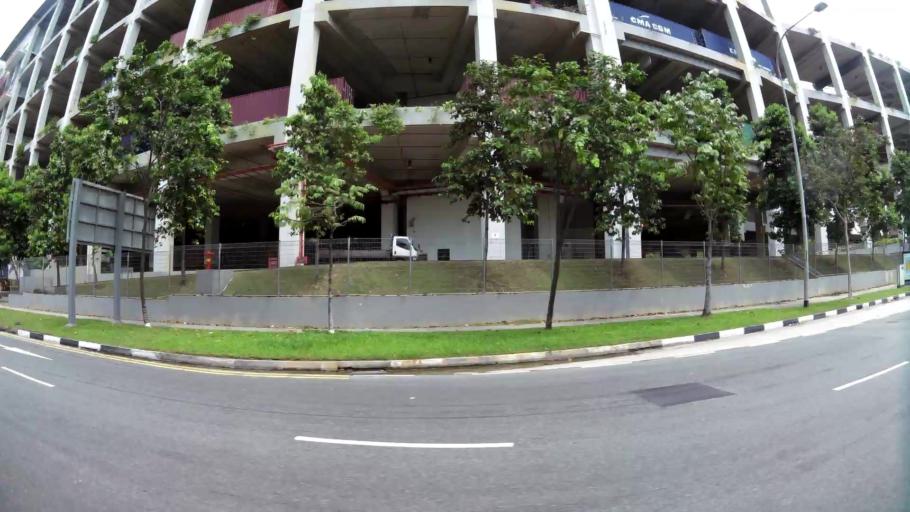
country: SG
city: Singapore
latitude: 1.3161
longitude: 103.7098
